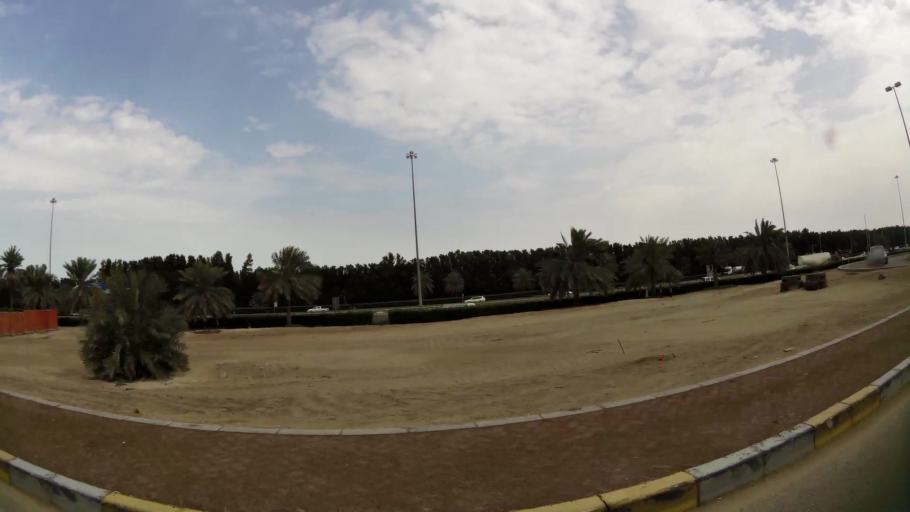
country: AE
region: Abu Dhabi
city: Abu Dhabi
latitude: 24.4305
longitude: 54.4671
